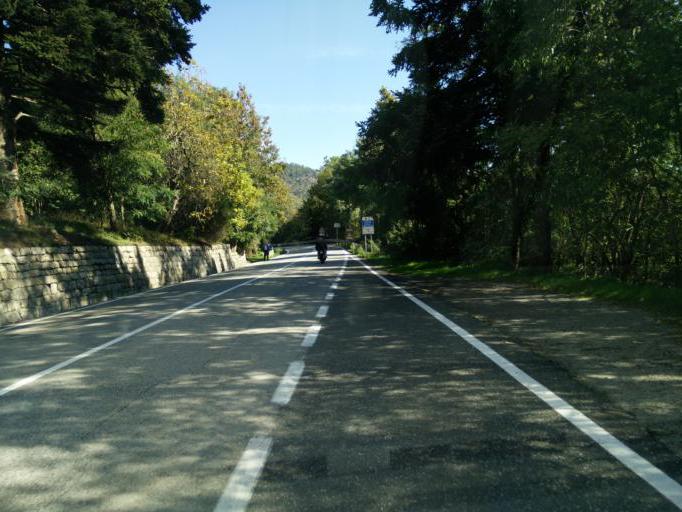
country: IT
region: Liguria
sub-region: Provincia di La Spezia
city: Framura
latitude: 44.2449
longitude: 9.5818
